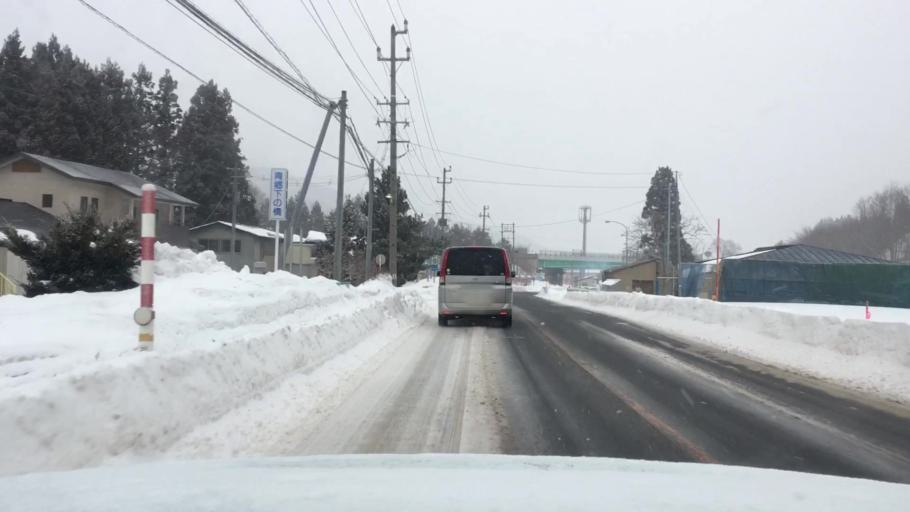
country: JP
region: Akita
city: Hanawa
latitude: 40.0446
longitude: 140.9994
